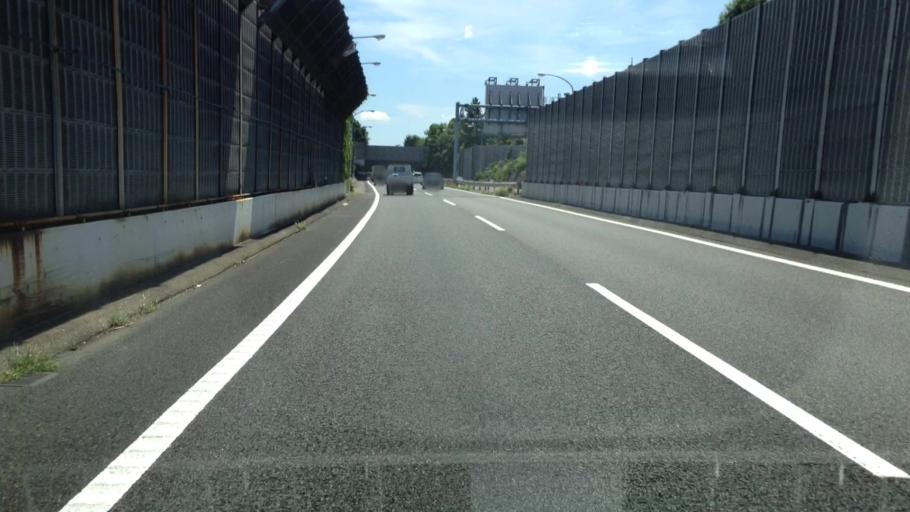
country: JP
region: Kanagawa
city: Yokohama
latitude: 35.4070
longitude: 139.5749
